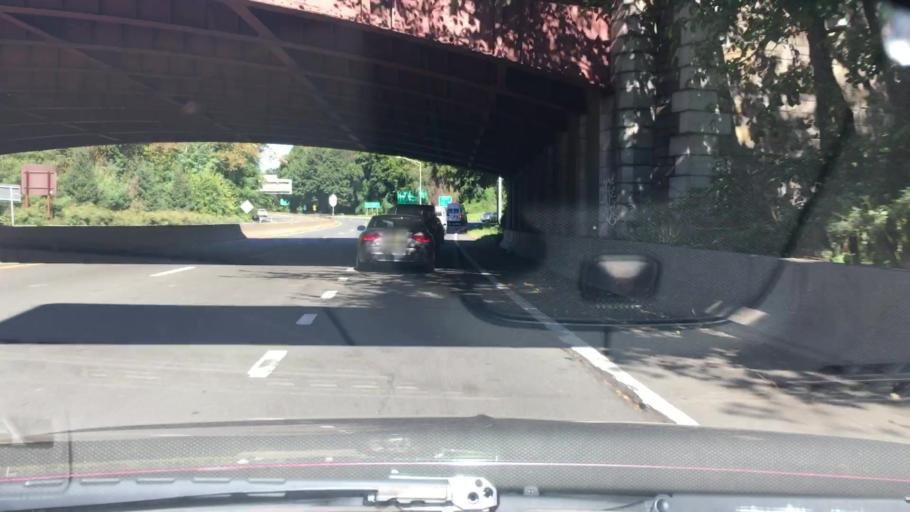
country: US
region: New York
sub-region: Westchester County
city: Pelham
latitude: 40.9213
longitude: -73.8097
